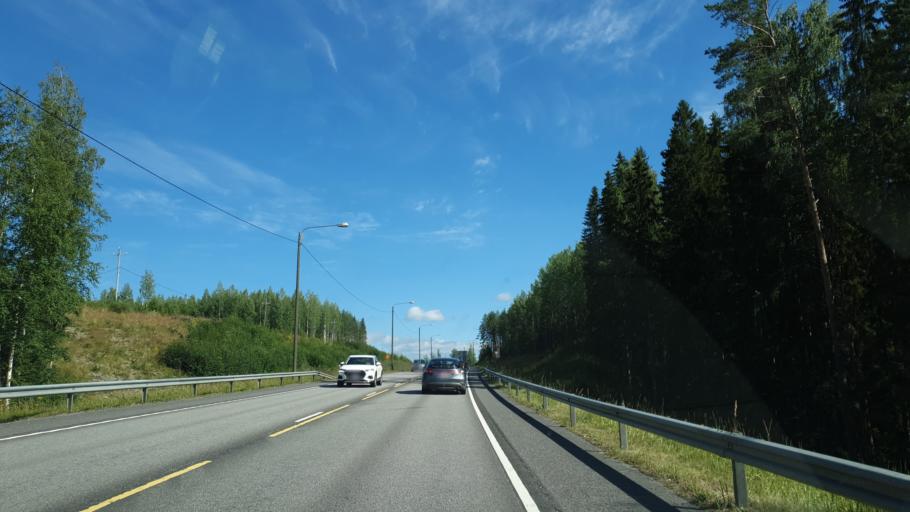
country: FI
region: Central Finland
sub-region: Jyvaeskylae
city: Toivakka
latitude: 62.2477
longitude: 26.0305
